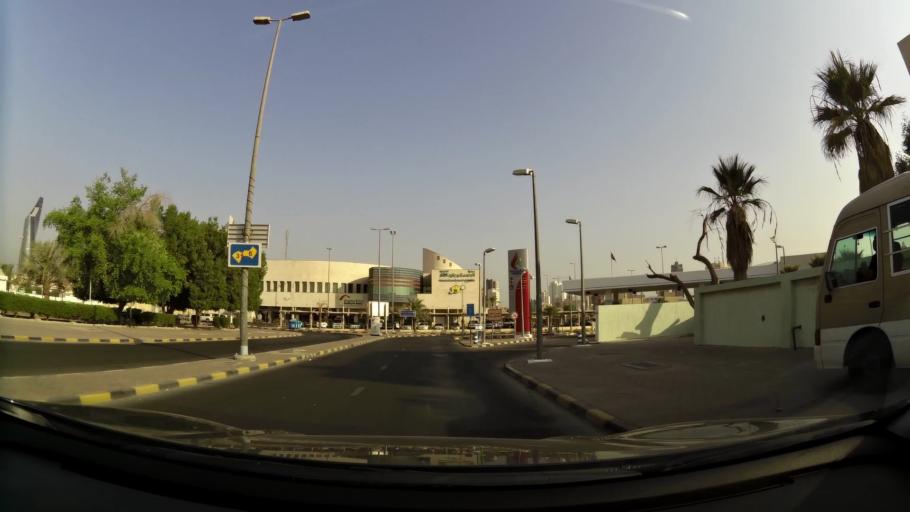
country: KW
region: Al Asimah
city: Ad Dasmah
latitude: 29.3644
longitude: 48.0013
